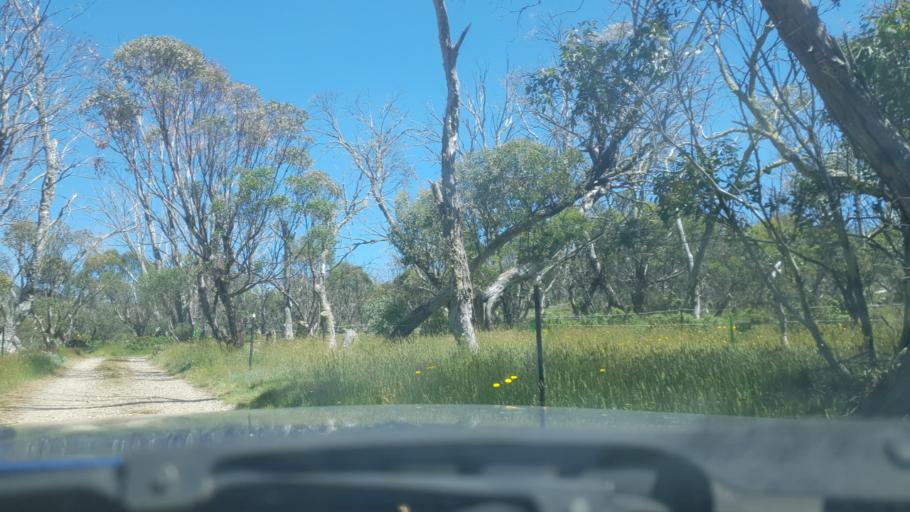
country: AU
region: Victoria
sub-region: Alpine
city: Mount Beauty
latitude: -36.9288
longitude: 147.3044
